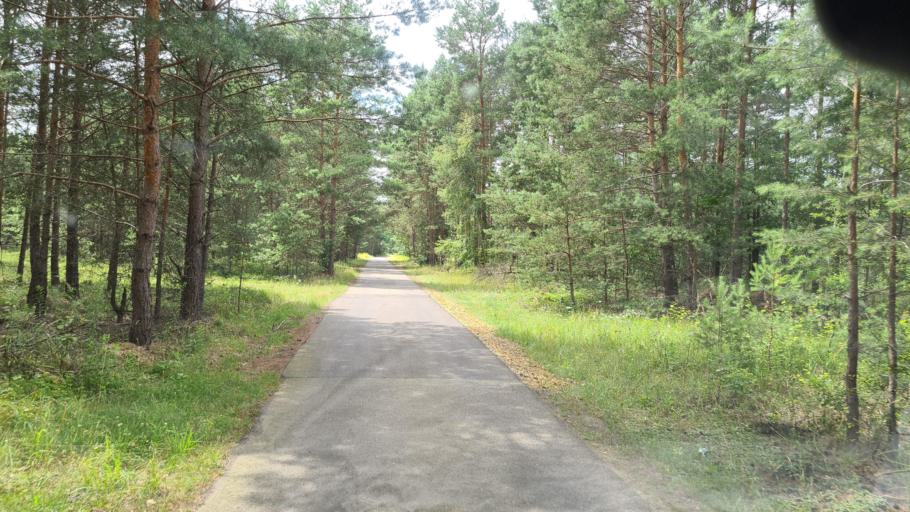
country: DE
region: Brandenburg
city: Grossraschen
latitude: 51.5968
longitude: 14.0277
